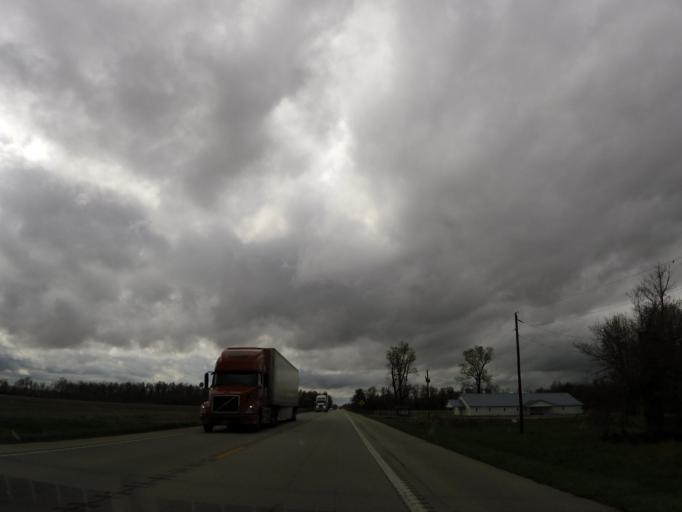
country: US
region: Missouri
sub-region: Butler County
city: Poplar Bluff
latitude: 36.6434
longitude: -90.5204
